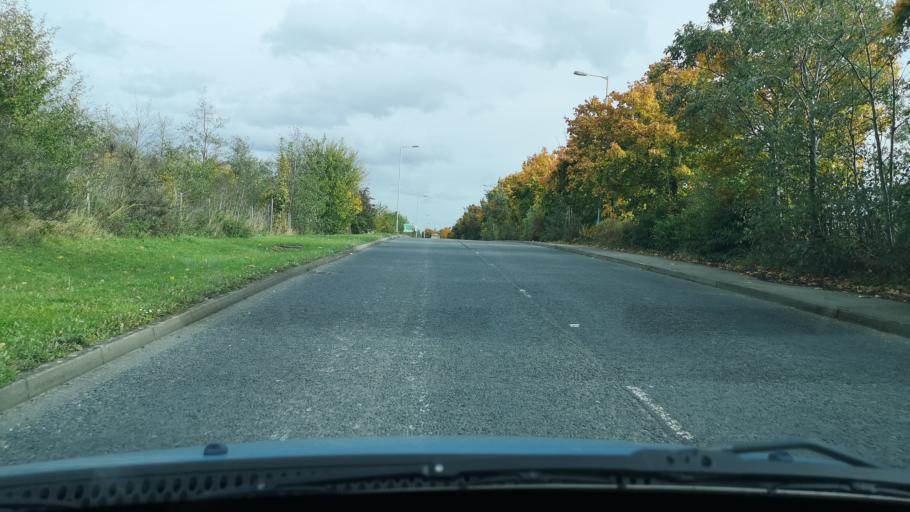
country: GB
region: England
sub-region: City and Borough of Wakefield
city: Featherstone
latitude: 53.6812
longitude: -1.3740
